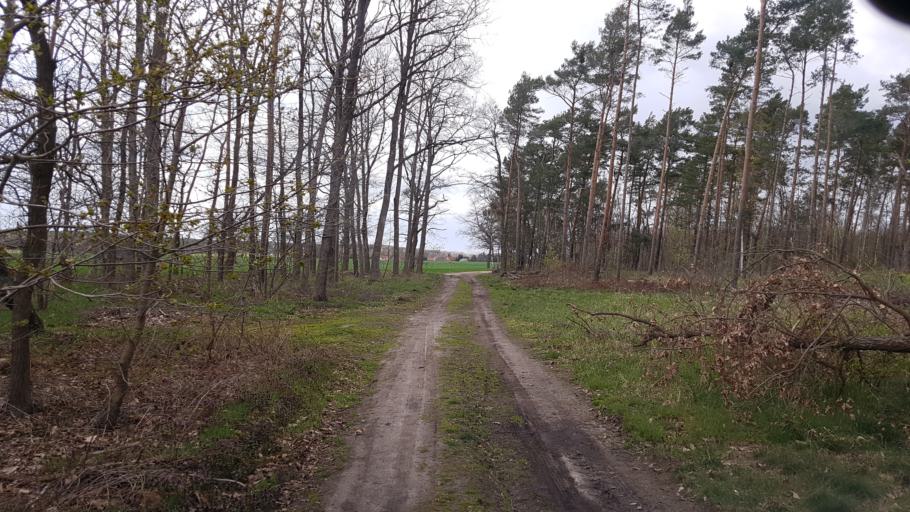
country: DE
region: Brandenburg
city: Calau
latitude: 51.7369
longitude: 13.9284
